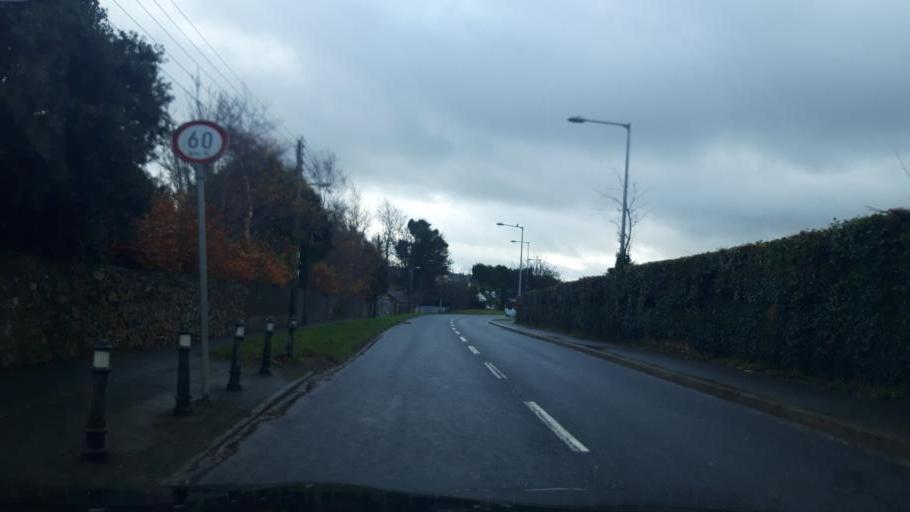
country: IE
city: Newtownmountkennedy
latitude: 53.0874
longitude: -6.1076
